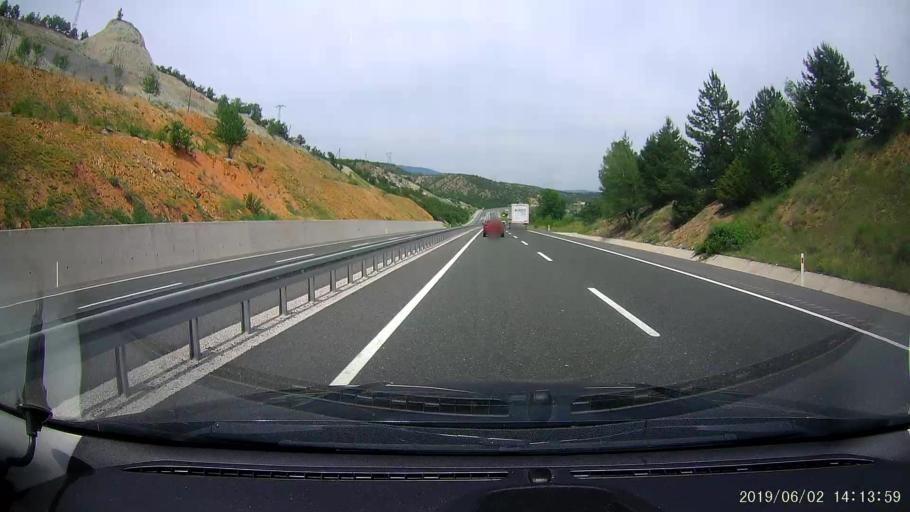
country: TR
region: Cankiri
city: Yaprakli
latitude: 40.9306
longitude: 33.8435
